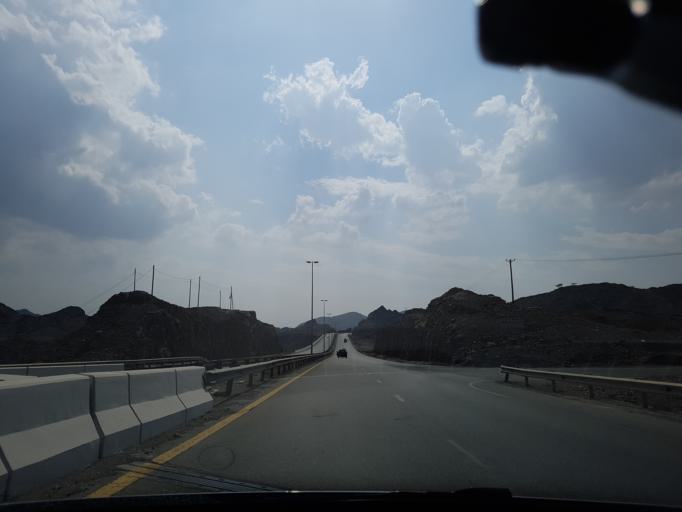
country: AE
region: Al Fujayrah
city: Dibba Al-Fujairah
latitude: 25.5298
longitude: 56.1182
